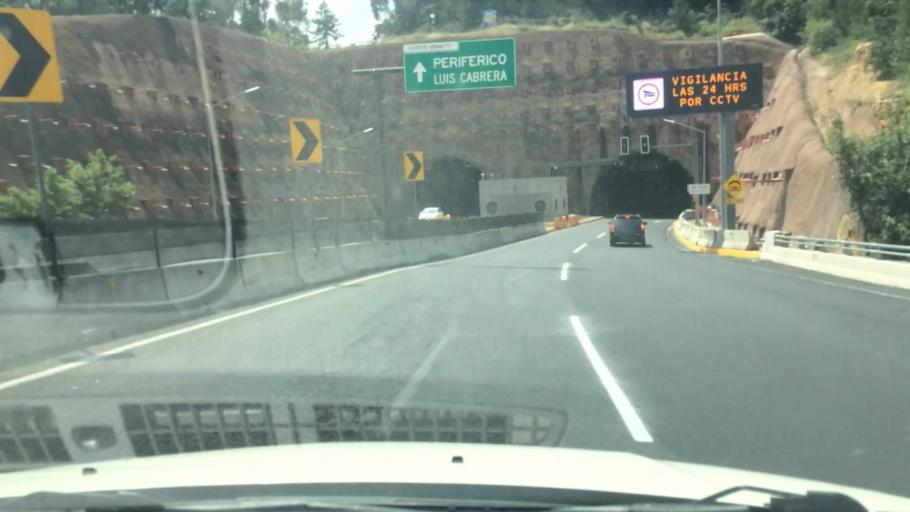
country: MX
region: Mexico City
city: Magdalena Contreras
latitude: 19.3315
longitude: -99.2372
